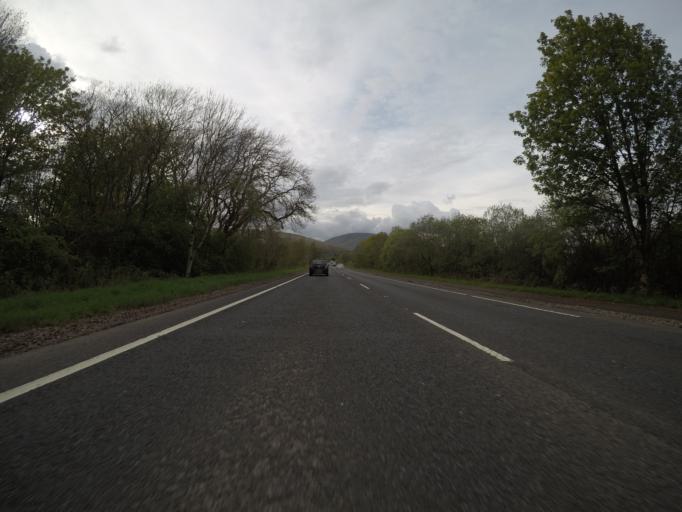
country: GB
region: Scotland
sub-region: West Dunbartonshire
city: Balloch
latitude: 56.0341
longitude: -4.6387
